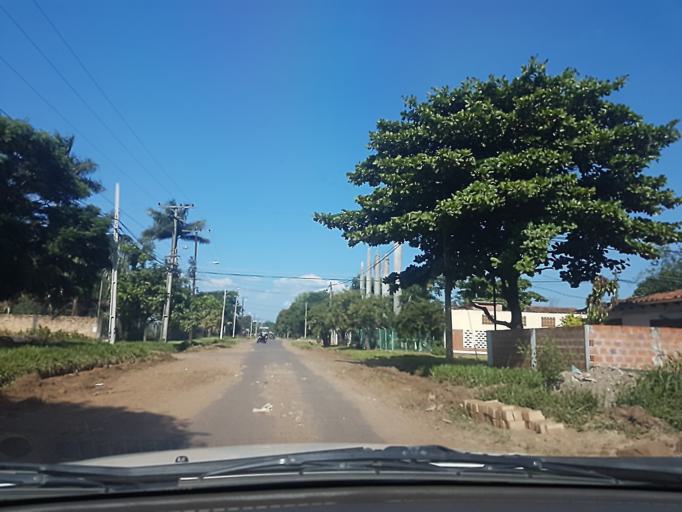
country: PY
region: Central
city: Limpio
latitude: -25.1750
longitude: -57.4804
